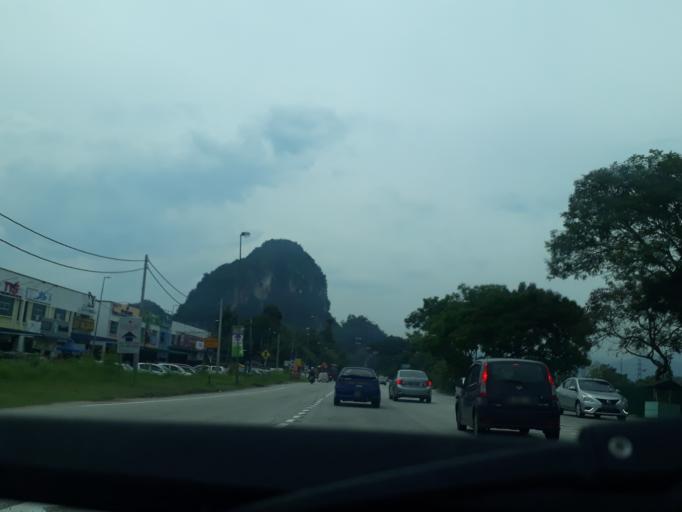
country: MY
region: Perak
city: Ipoh
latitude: 4.6354
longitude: 101.1545
